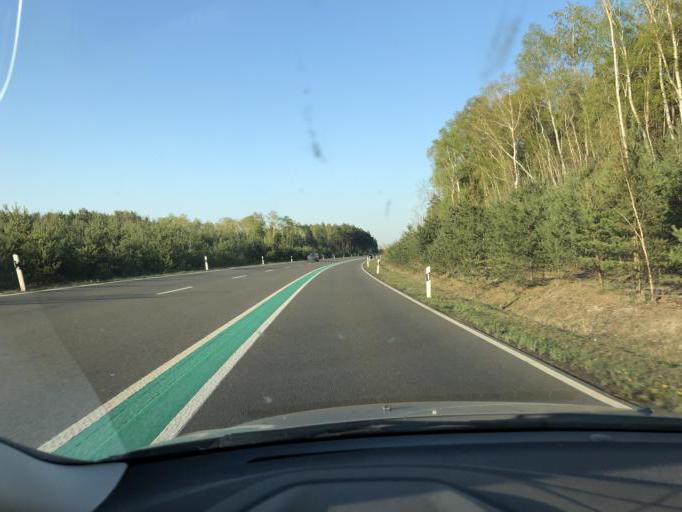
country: DE
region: Brandenburg
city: Schwarzbach
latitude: 51.4947
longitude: 13.9449
